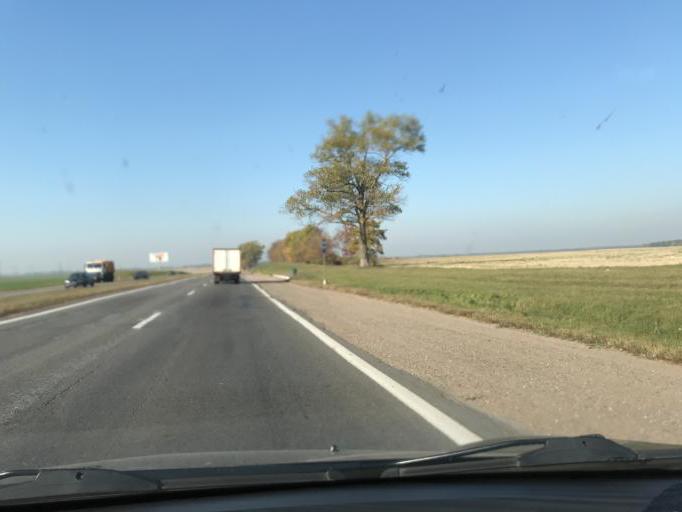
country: BY
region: Minsk
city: Dukora
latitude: 53.6845
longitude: 27.9151
